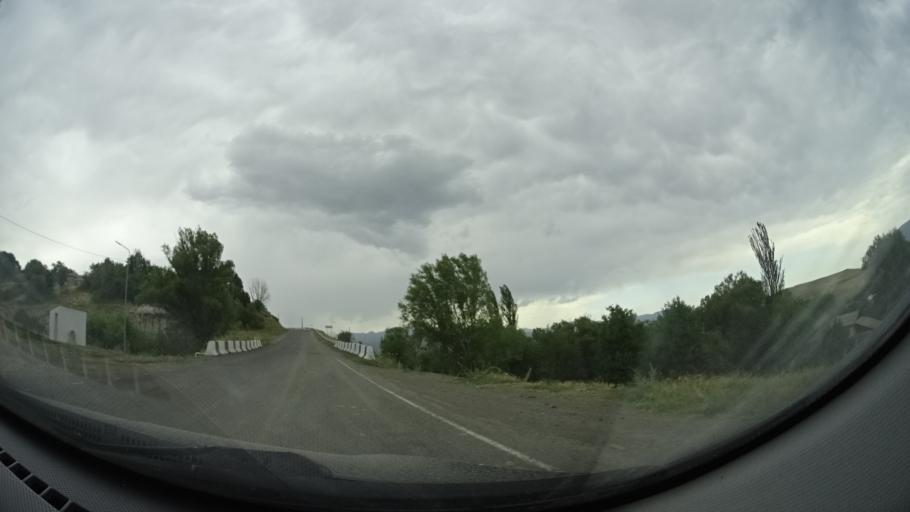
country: GE
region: Samtskhe-Javakheti
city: Akhaltsikhe
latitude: 41.6329
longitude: 43.0437
